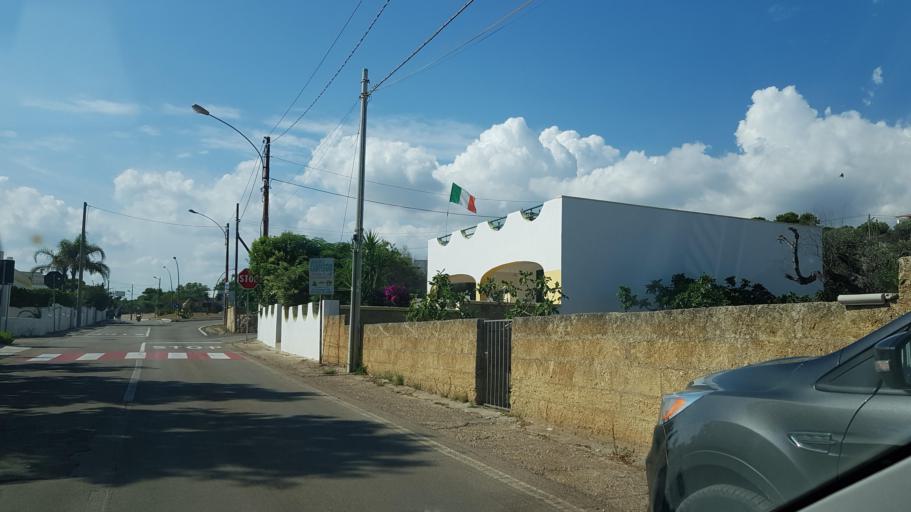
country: IT
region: Apulia
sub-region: Provincia di Lecce
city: Morciano di Leuca
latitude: 39.8140
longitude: 18.3140
